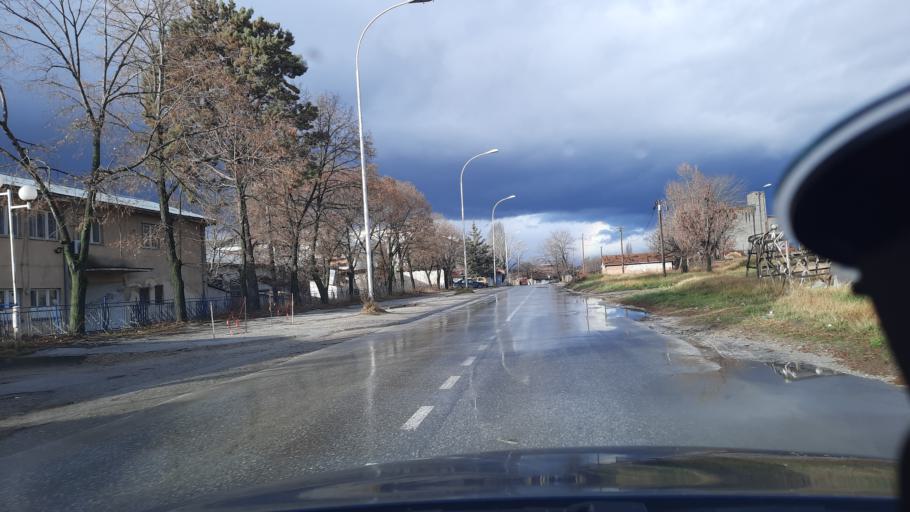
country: MK
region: Prilep
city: Markov Grad
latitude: 41.3435
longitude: 21.5381
